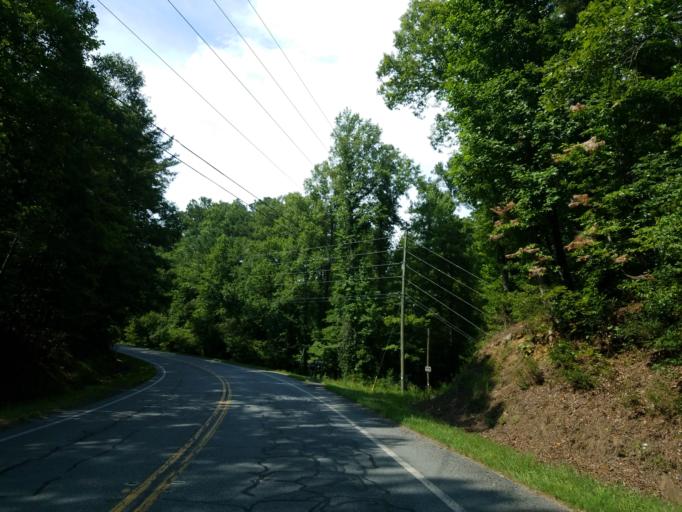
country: US
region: Georgia
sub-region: Gilmer County
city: Ellijay
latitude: 34.5997
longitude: -84.5931
